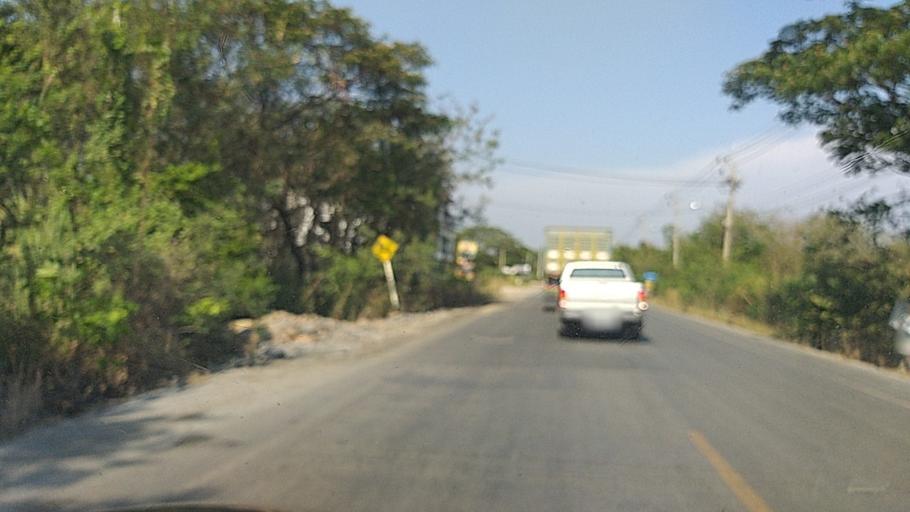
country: TH
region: Nonthaburi
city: Bang Yai
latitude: 13.8780
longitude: 100.2991
